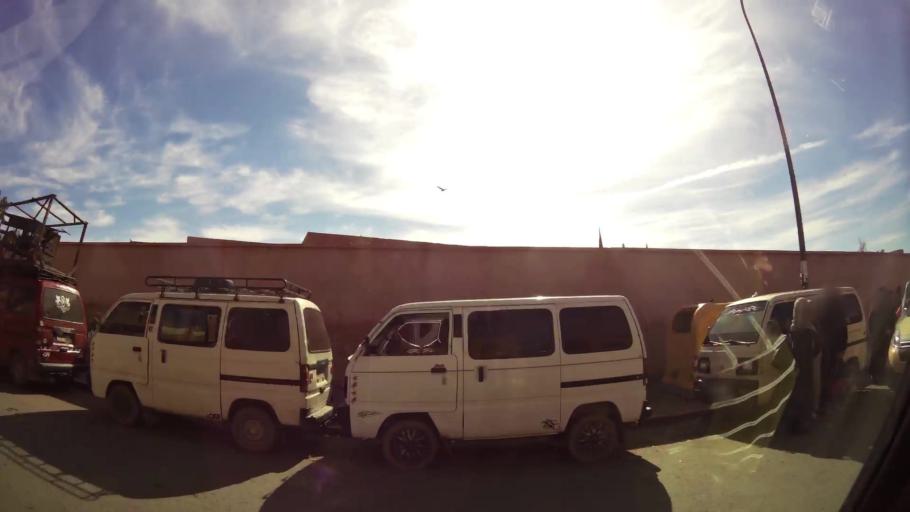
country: MA
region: Marrakech-Tensift-Al Haouz
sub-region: Marrakech
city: Marrakesh
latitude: 31.6075
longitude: -7.9641
